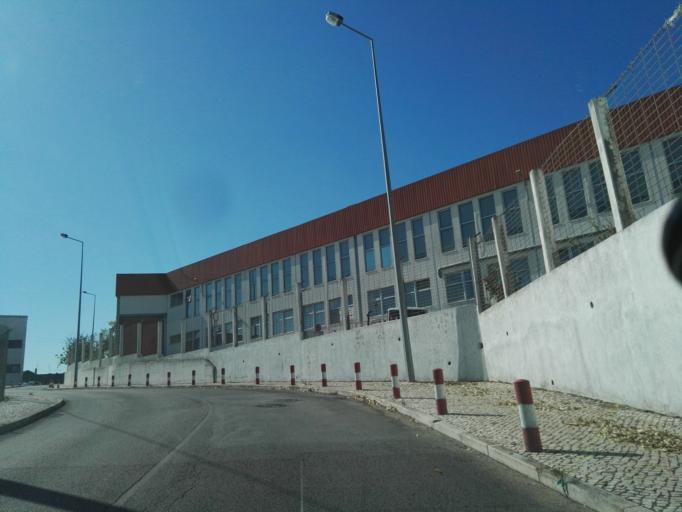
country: PT
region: Lisbon
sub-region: Loures
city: Camarate
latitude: 38.7892
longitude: -9.1270
